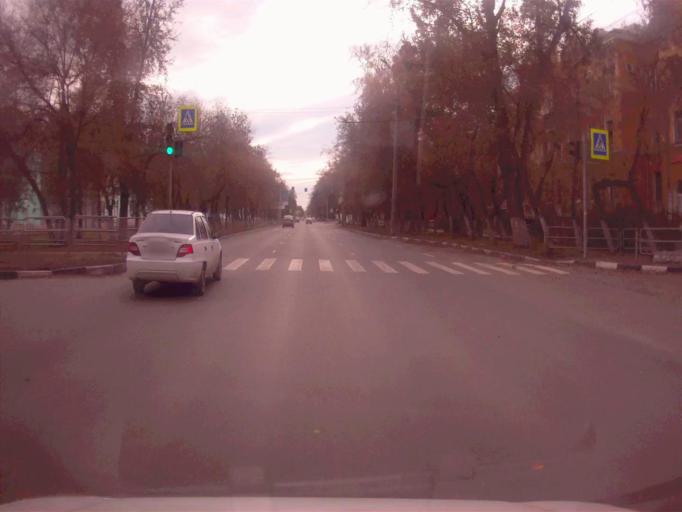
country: RU
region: Chelyabinsk
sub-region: Gorod Chelyabinsk
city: Chelyabinsk
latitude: 55.1226
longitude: 61.4736
